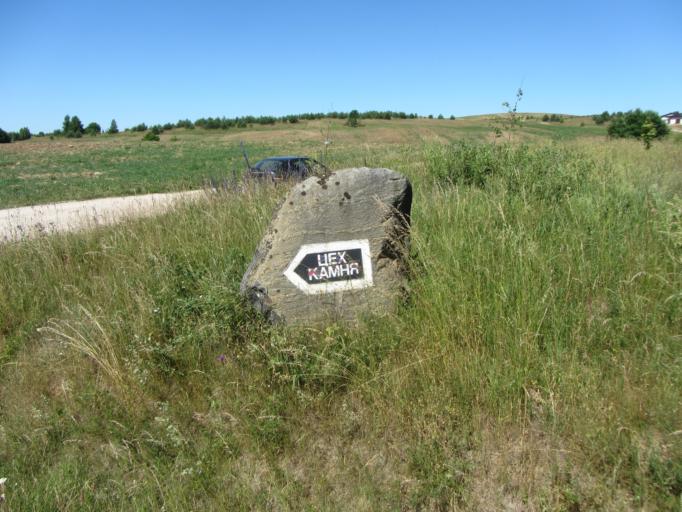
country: LT
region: Vilnius County
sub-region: Vilniaus Rajonas
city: Vievis
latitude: 54.6432
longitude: 24.8072
